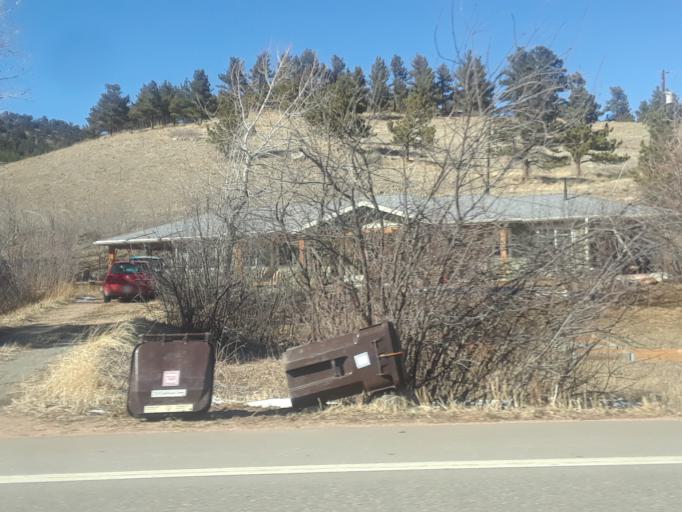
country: US
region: Colorado
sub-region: Boulder County
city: Lyons
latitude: 40.1328
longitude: -105.2893
